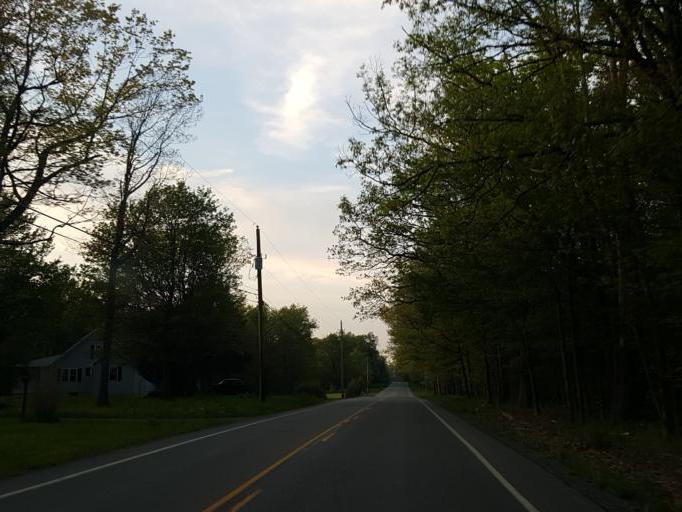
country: US
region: Pennsylvania
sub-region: Cambria County
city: Gallitzin
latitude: 40.5024
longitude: -78.5404
